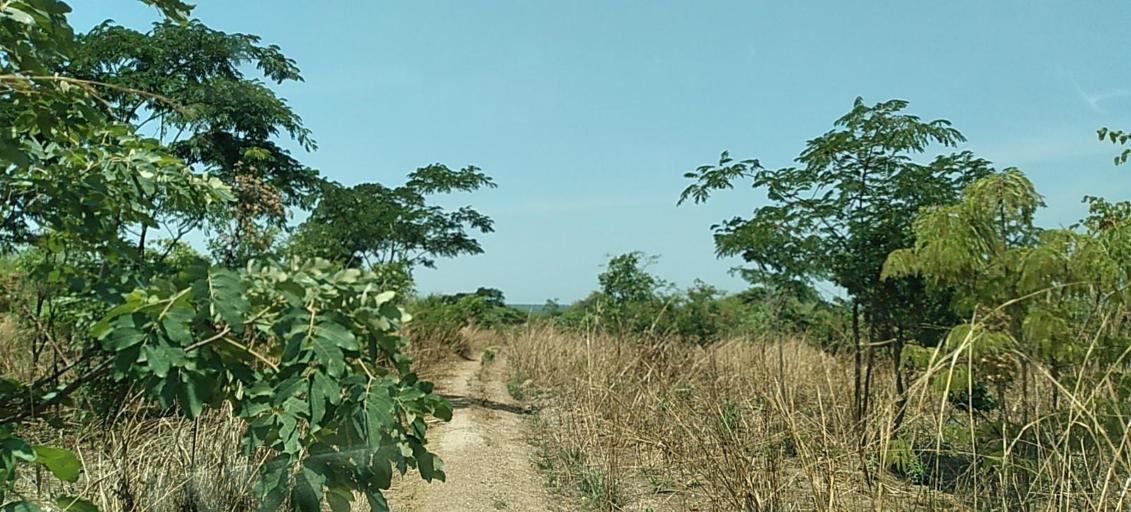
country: ZM
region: Copperbelt
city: Luanshya
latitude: -12.9837
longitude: 28.3283
